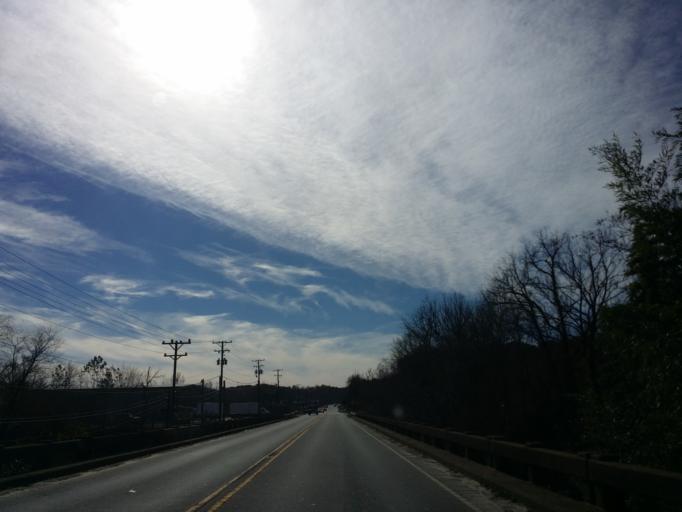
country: US
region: North Carolina
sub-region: McDowell County
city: Marion
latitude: 35.6986
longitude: -82.0469
